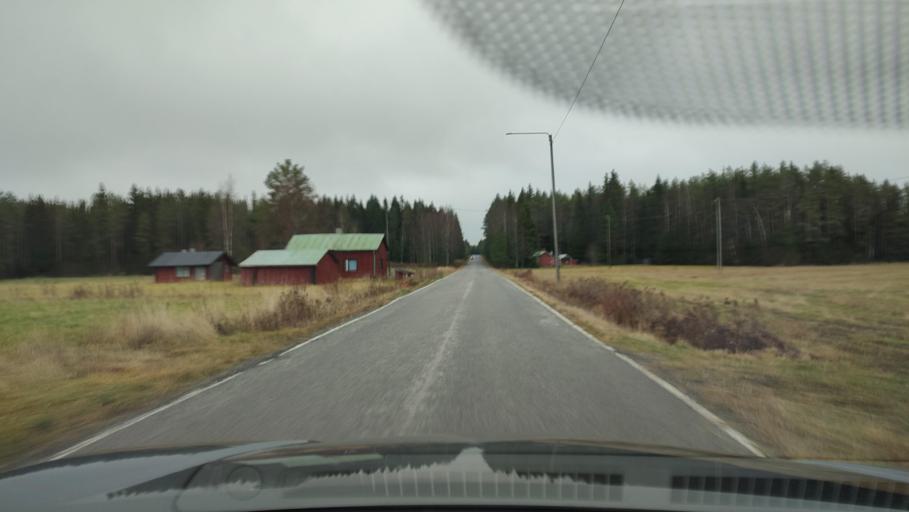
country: FI
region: Southern Ostrobothnia
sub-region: Suupohja
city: Isojoki
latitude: 62.1845
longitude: 21.9332
